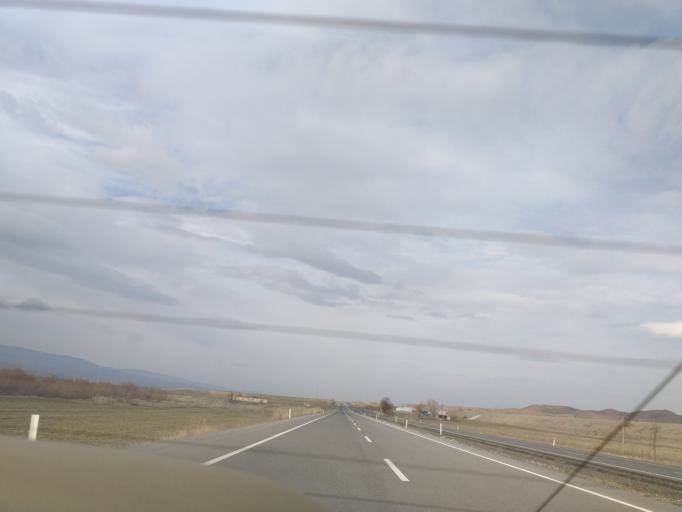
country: TR
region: Kirsehir
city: Mecidiye
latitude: 39.7033
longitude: 34.3831
